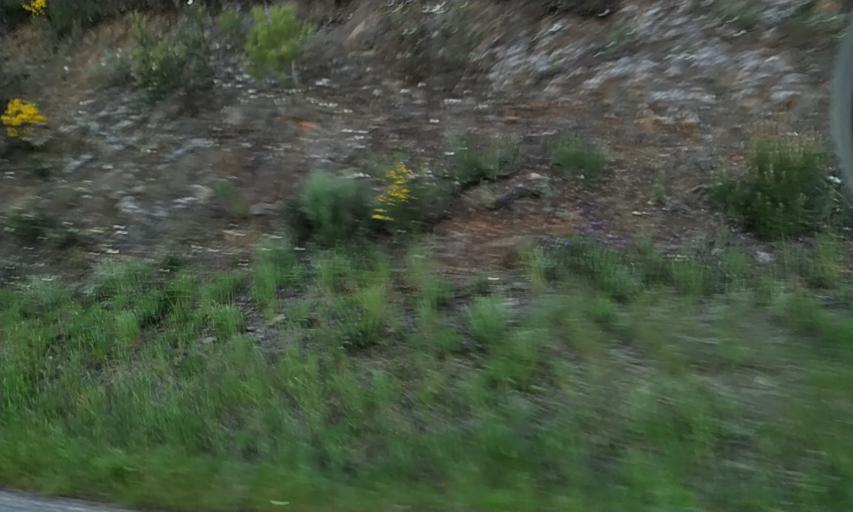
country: PT
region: Portalegre
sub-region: Portalegre
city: Sao Juliao
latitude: 39.3596
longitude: -7.3194
